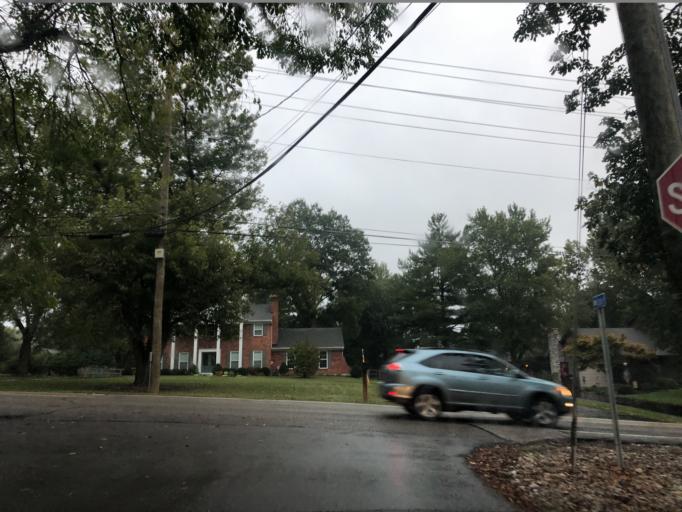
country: US
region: Ohio
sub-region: Hamilton County
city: Montgomery
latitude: 39.2299
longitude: -84.3223
